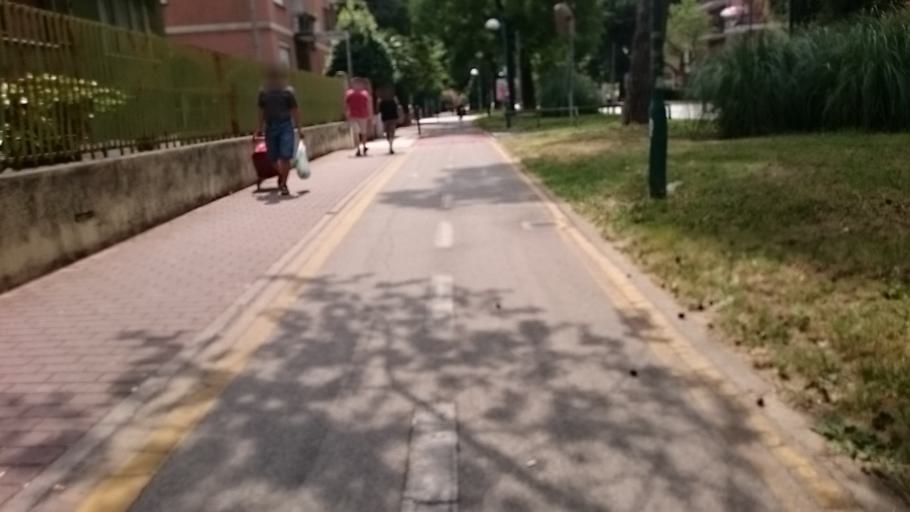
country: IT
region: Veneto
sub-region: Provincia di Venezia
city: Mestre
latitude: 45.4885
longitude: 12.2537
